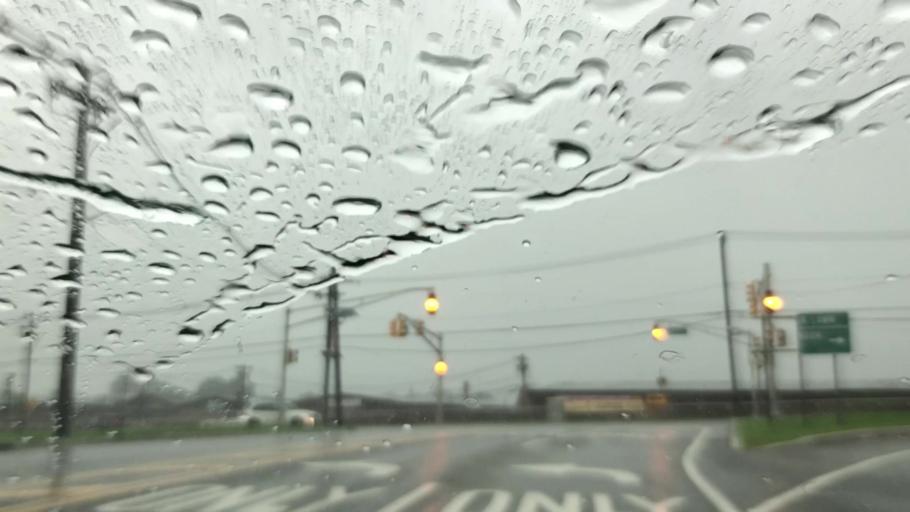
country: US
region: New Jersey
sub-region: Bergen County
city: Elmwood Park
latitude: 40.9060
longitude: -74.1064
